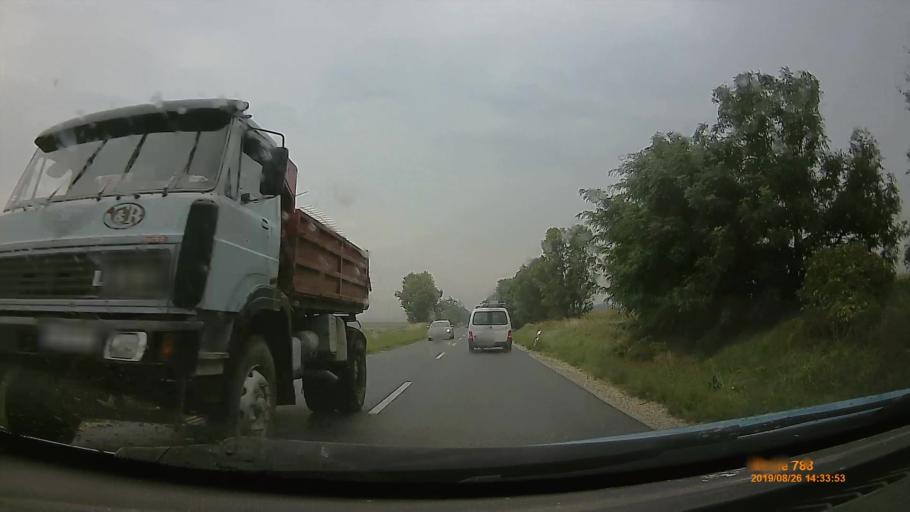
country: HU
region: Fejer
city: Zamoly
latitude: 47.2672
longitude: 18.4197
